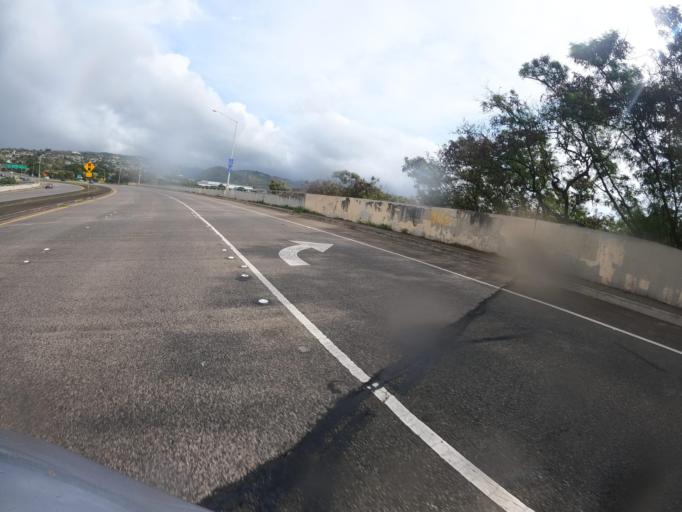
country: US
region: Hawaii
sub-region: Honolulu County
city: Halawa
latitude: 21.3694
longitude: -157.9205
